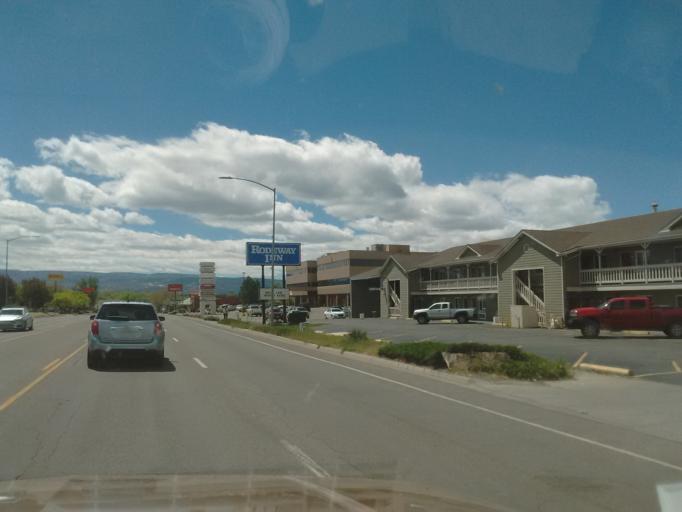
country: US
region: Colorado
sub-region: Mesa County
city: Grand Junction
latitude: 39.1094
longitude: -108.5423
